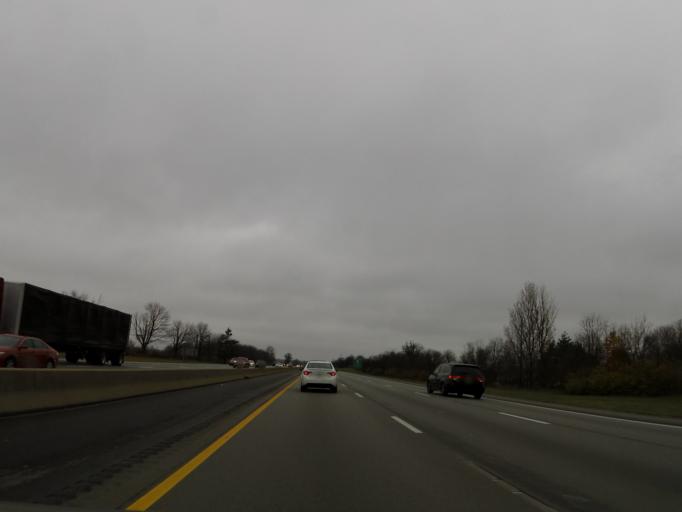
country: US
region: Kentucky
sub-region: Scott County
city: Georgetown
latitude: 38.1829
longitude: -84.5295
